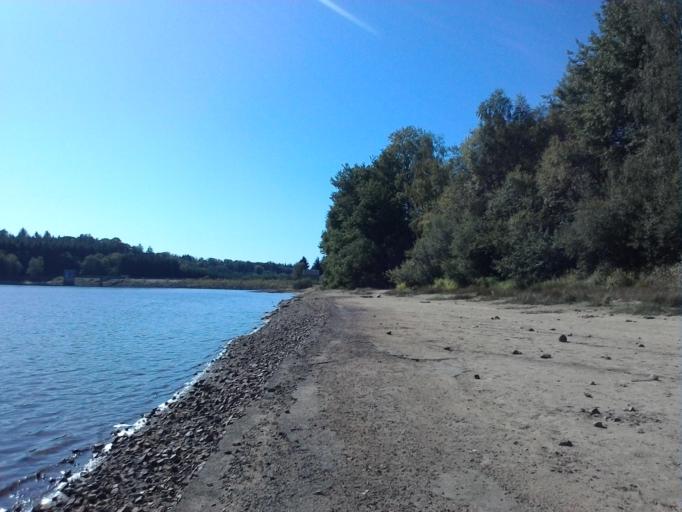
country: FR
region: Bourgogne
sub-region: Departement de la Cote-d'Or
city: Saulieu
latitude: 47.2483
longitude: 4.1885
